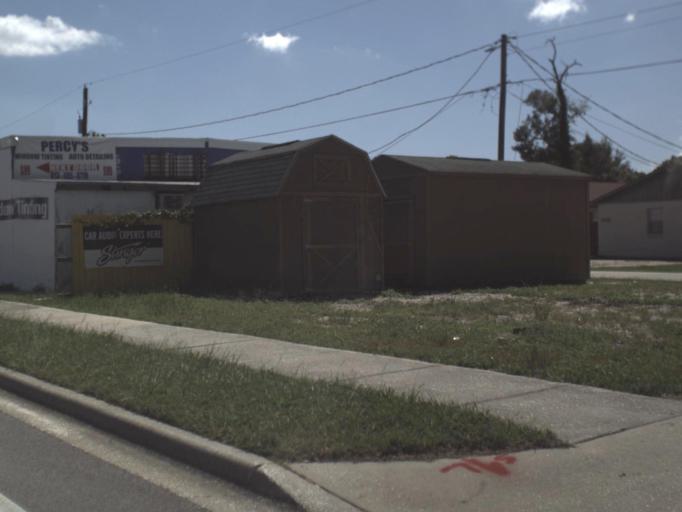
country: US
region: Florida
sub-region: Hillsborough County
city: Tampa
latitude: 27.8745
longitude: -82.5065
